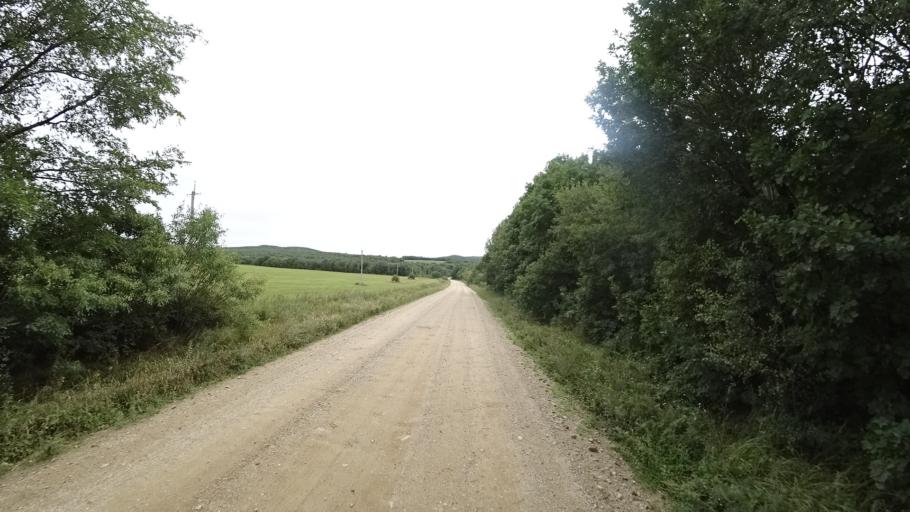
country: RU
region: Primorskiy
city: Lyalichi
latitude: 44.0699
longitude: 132.4770
